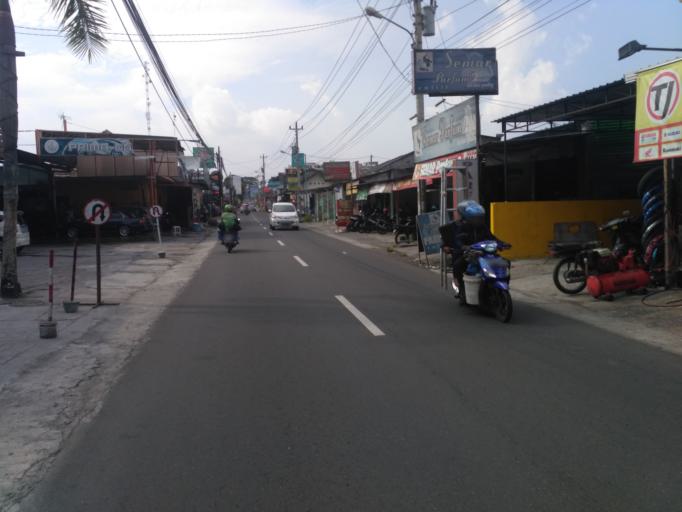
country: ID
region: Daerah Istimewa Yogyakarta
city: Depok
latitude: -7.7762
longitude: 110.4085
